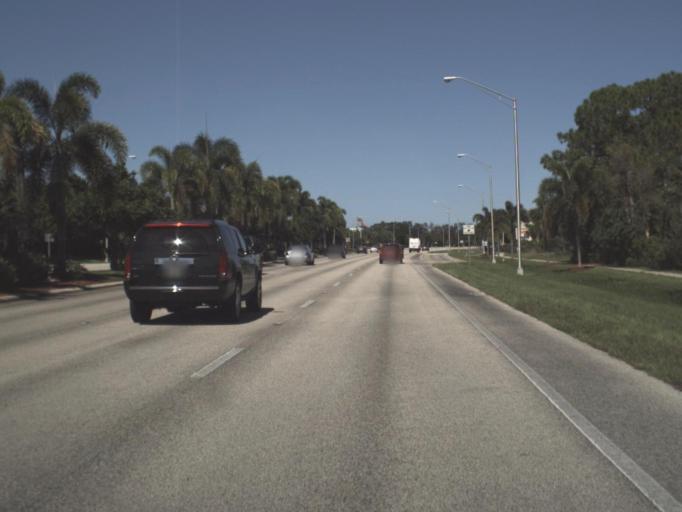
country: US
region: Florida
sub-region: Collier County
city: Naples Park
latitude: 26.3020
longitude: -81.8035
